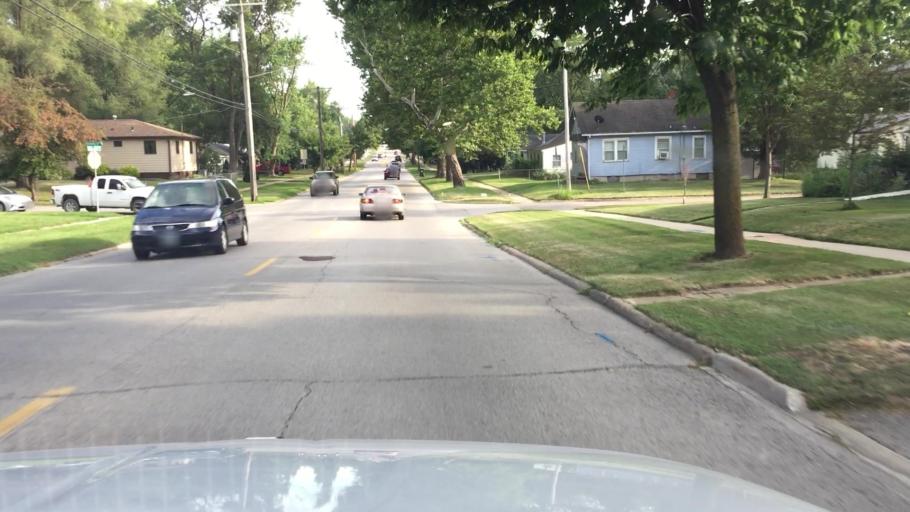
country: US
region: Iowa
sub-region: Johnson County
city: Iowa City
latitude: 41.6542
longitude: -91.5020
